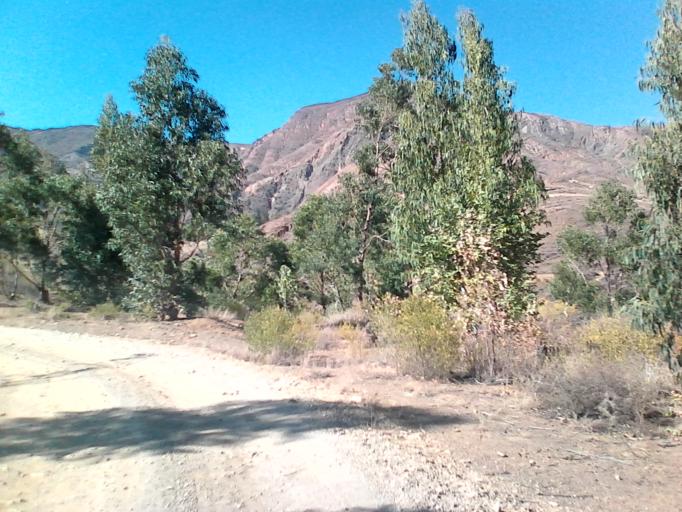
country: CO
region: Boyaca
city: Sachica
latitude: 5.5632
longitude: -73.5483
